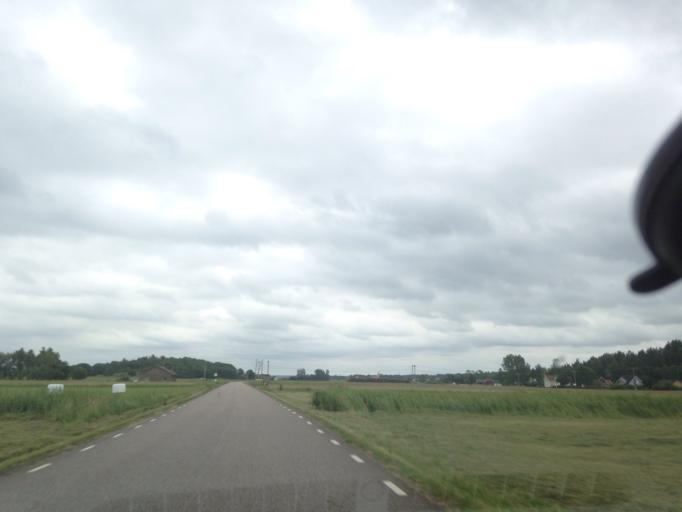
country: SE
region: Vaestra Goetaland
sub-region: Kungalvs Kommun
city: Kode
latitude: 57.8301
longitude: 11.8086
